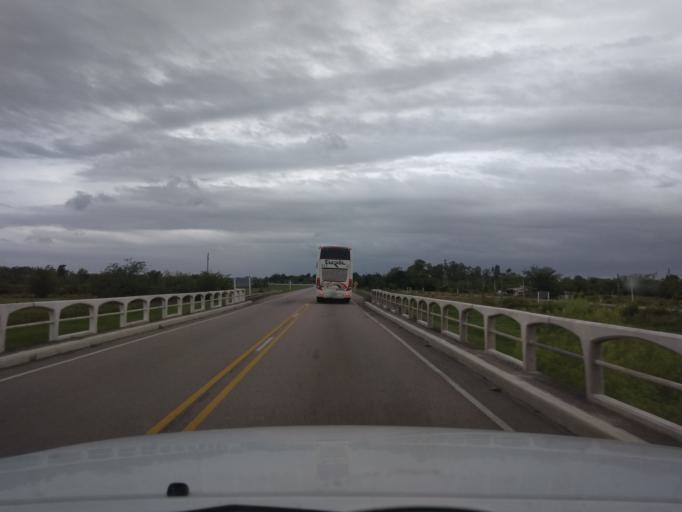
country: UY
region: Canelones
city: Canelones
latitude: -34.5027
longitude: -56.2816
